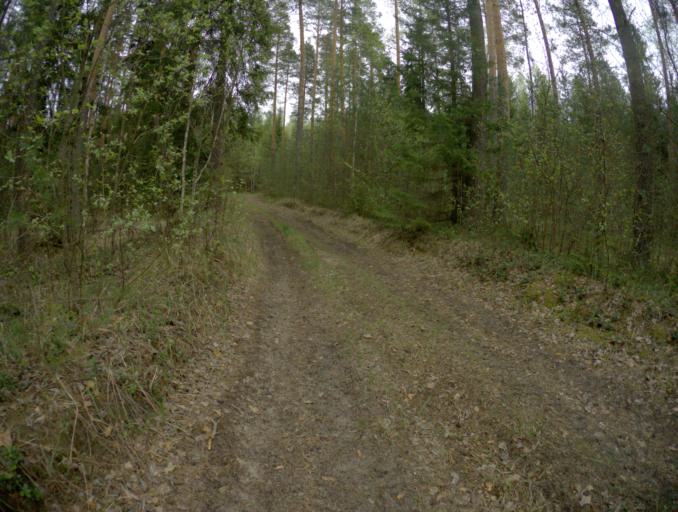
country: RU
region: Vladimir
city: Golovino
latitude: 55.8877
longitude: 40.4005
